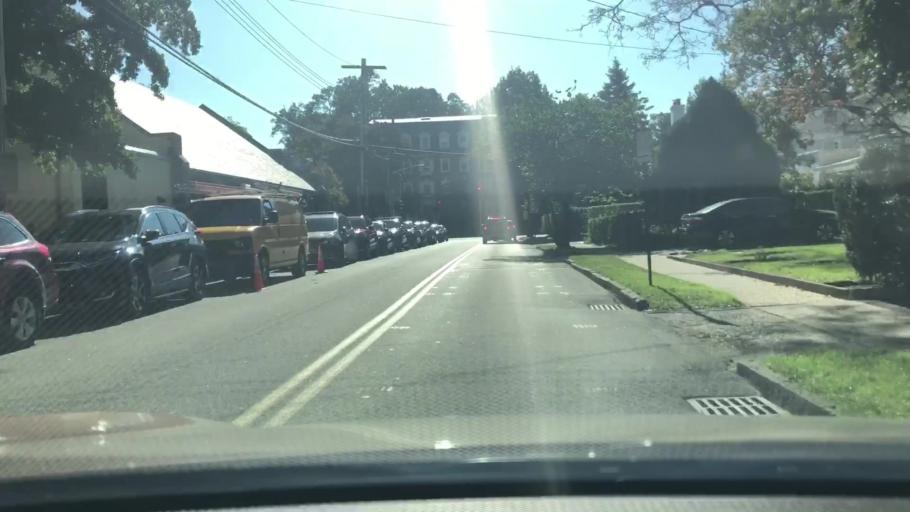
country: US
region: New York
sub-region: Westchester County
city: Bronxville
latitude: 40.9364
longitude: -73.8335
